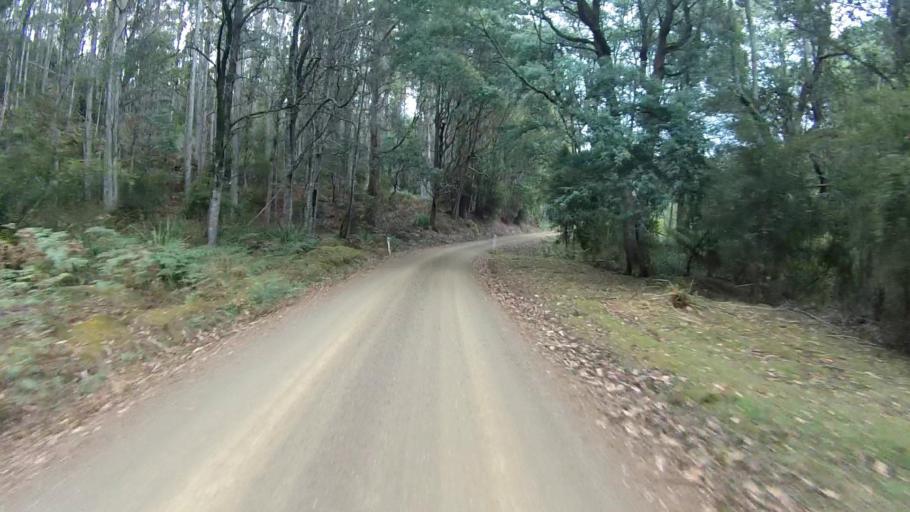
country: AU
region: Tasmania
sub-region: Kingborough
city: Kettering
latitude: -43.2127
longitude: 147.1788
